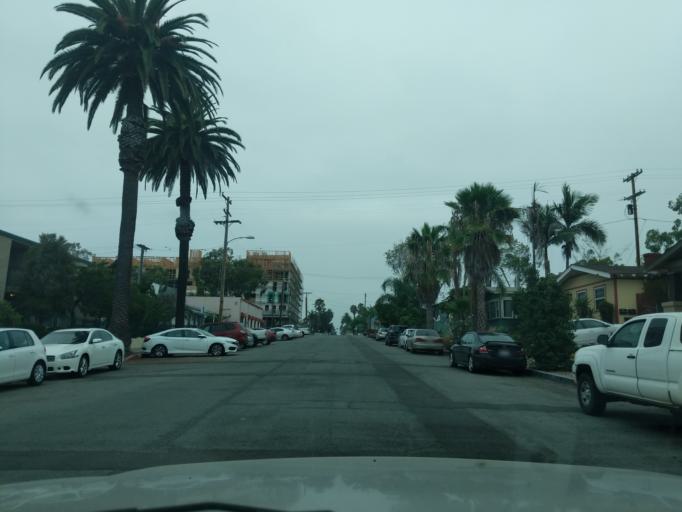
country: US
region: California
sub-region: San Diego County
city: San Diego
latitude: 32.7542
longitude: -117.1425
